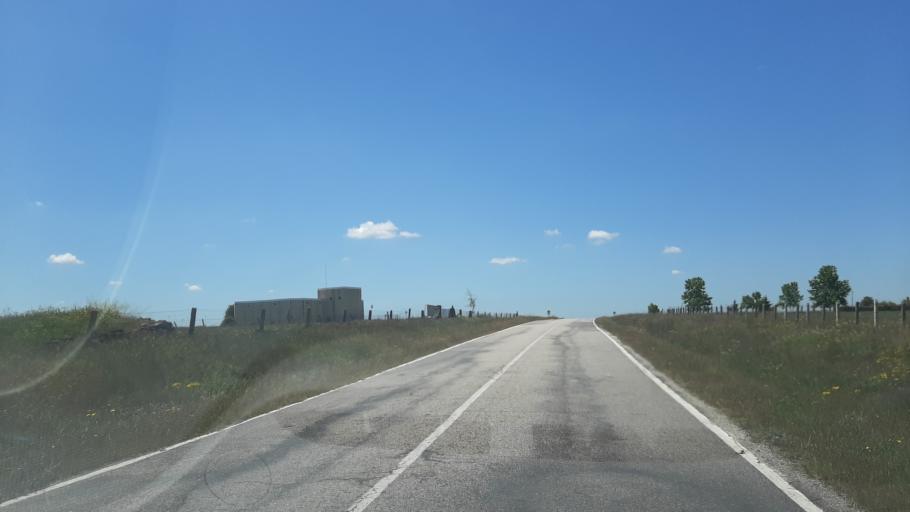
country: ES
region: Castille and Leon
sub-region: Provincia de Salamanca
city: Vitigudino
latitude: 41.0189
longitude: -6.4186
